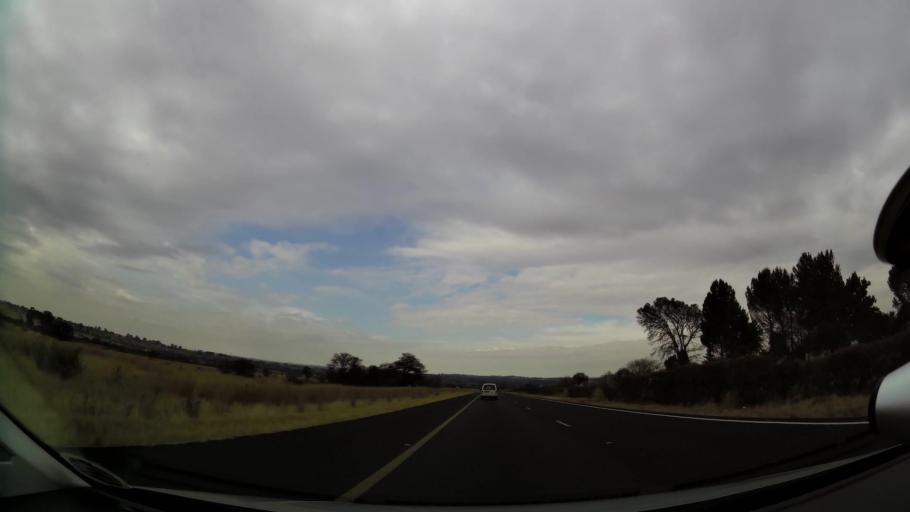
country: ZA
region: Orange Free State
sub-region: Fezile Dabi District Municipality
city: Kroonstad
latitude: -27.6410
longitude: 27.2477
